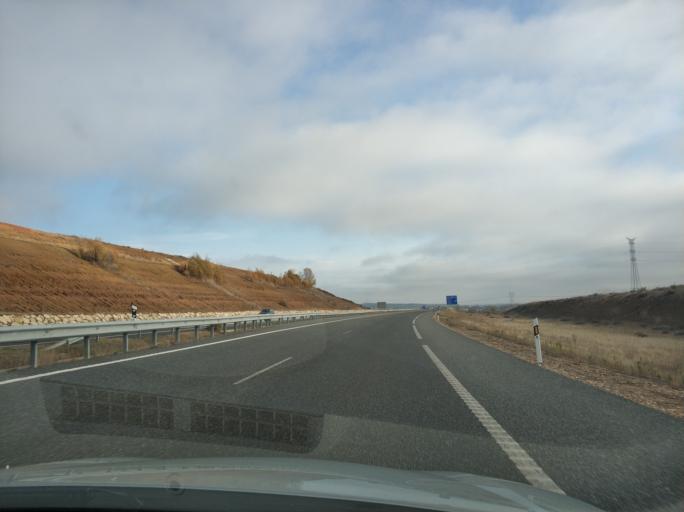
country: ES
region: Castille and Leon
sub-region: Provincia de Leon
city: Valdefresno
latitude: 42.5614
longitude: -5.4761
